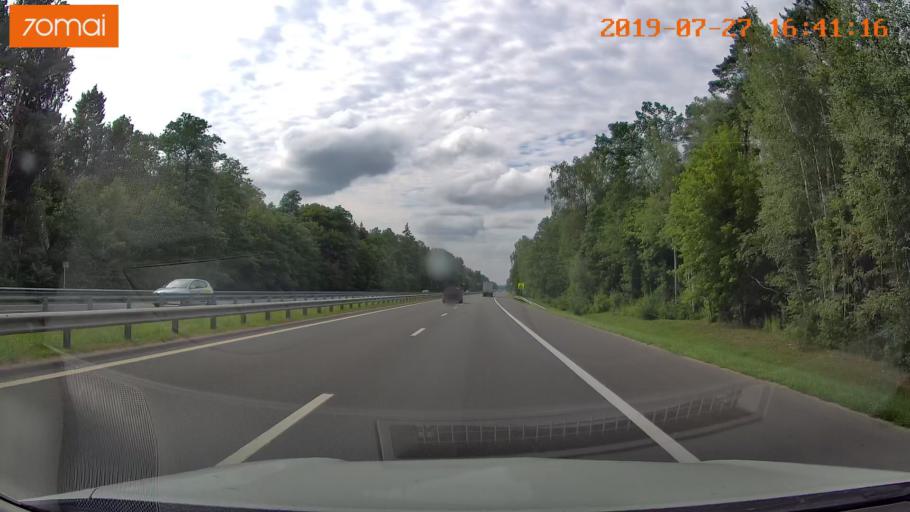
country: RU
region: Kaliningrad
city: Gvardeysk
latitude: 54.6540
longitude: 21.1514
